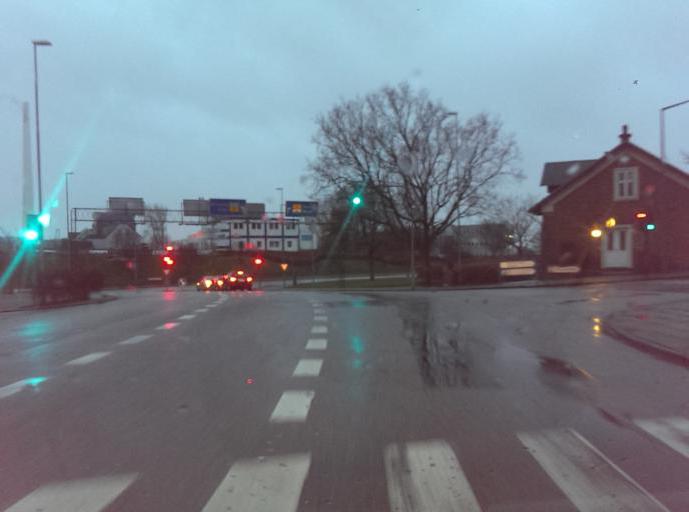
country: DK
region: South Denmark
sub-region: Esbjerg Kommune
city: Esbjerg
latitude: 55.4644
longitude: 8.4564
